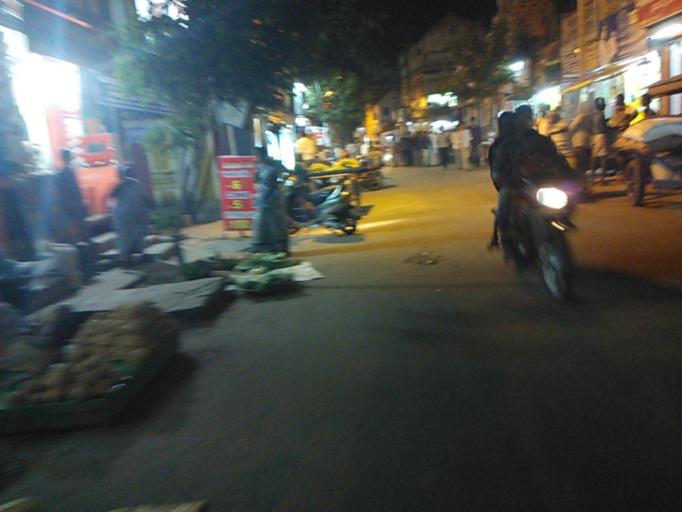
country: IN
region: Tamil Nadu
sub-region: Tiruchchirappalli
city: Tiruchirappalli
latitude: 10.8269
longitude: 78.6999
